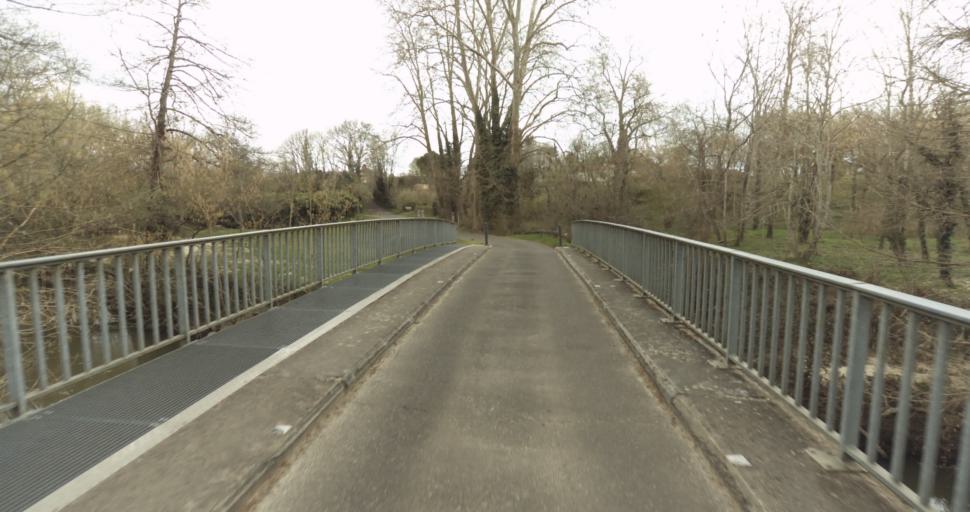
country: FR
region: Aquitaine
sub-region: Departement des Landes
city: Roquefort
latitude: 44.0309
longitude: -0.3181
